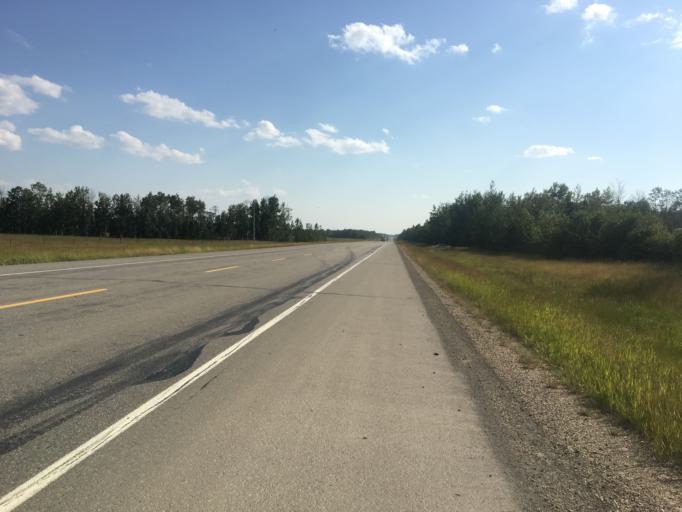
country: CA
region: Alberta
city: Sexsmith
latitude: 55.4507
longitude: -118.6702
